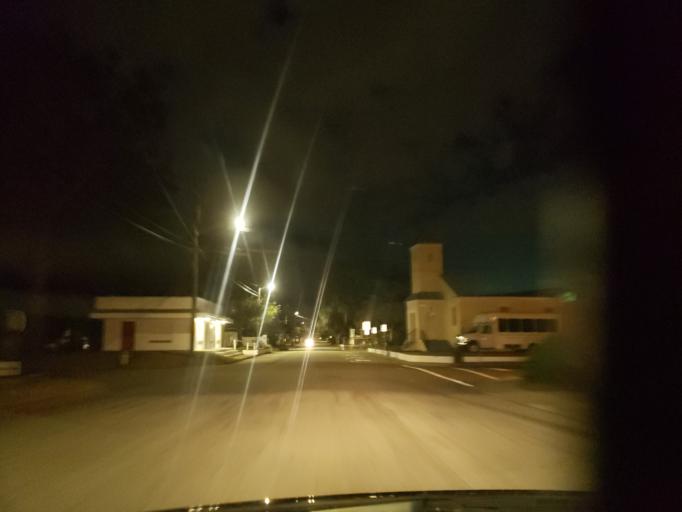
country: US
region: Georgia
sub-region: Chatham County
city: Thunderbolt
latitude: 32.0593
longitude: -81.0564
